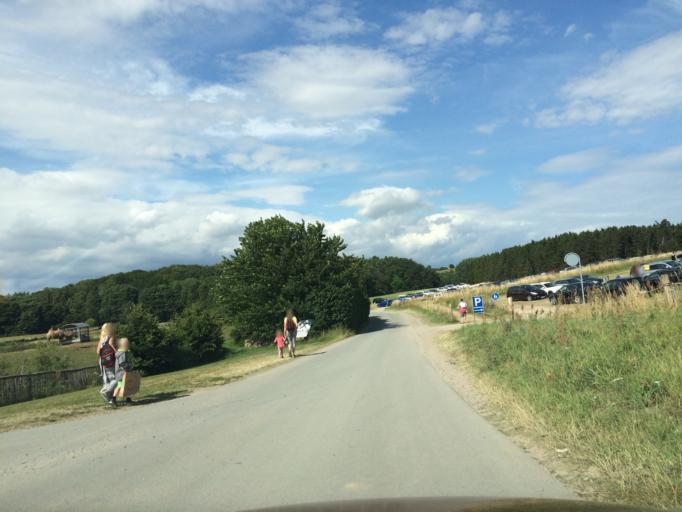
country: DK
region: Central Jutland
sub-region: Syddjurs Kommune
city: Ebeltoft
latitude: 56.2637
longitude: 10.7419
